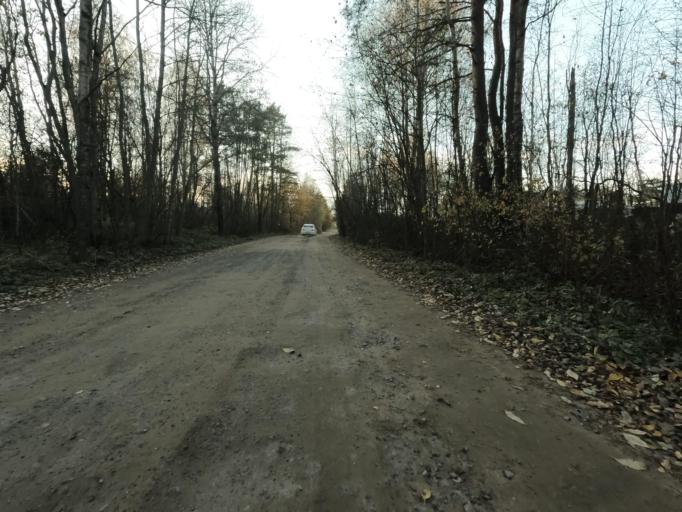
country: RU
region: Leningrad
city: Mga
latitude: 59.7609
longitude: 31.2601
